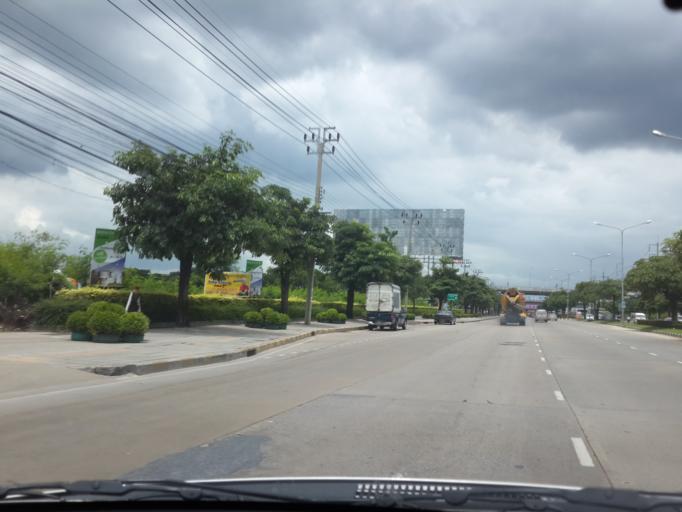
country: TH
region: Bangkok
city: Min Buri
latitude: 13.8150
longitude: 100.7416
